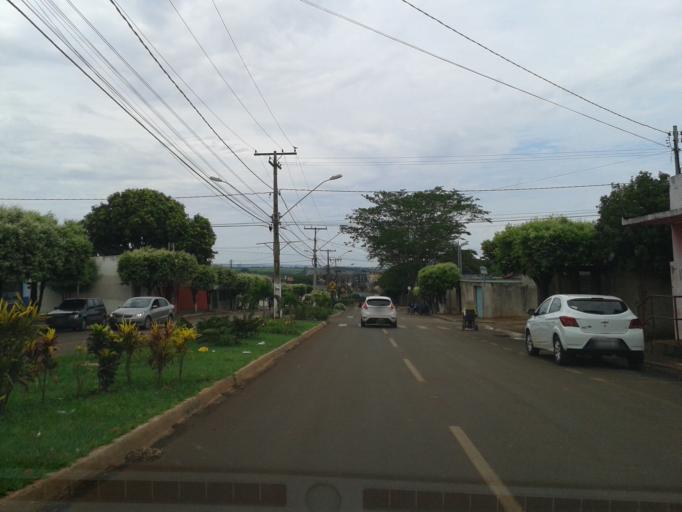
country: BR
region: Goias
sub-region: Itumbiara
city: Itumbiara
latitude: -18.4330
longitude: -49.1884
